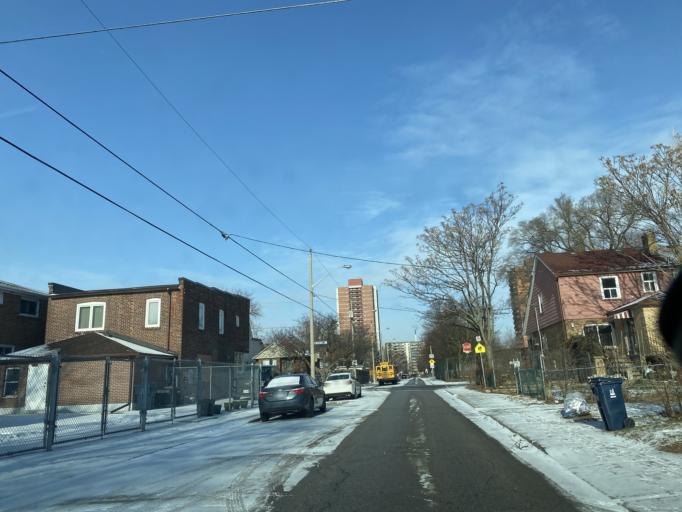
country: CA
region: Ontario
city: Toronto
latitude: 43.6852
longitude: -79.3520
